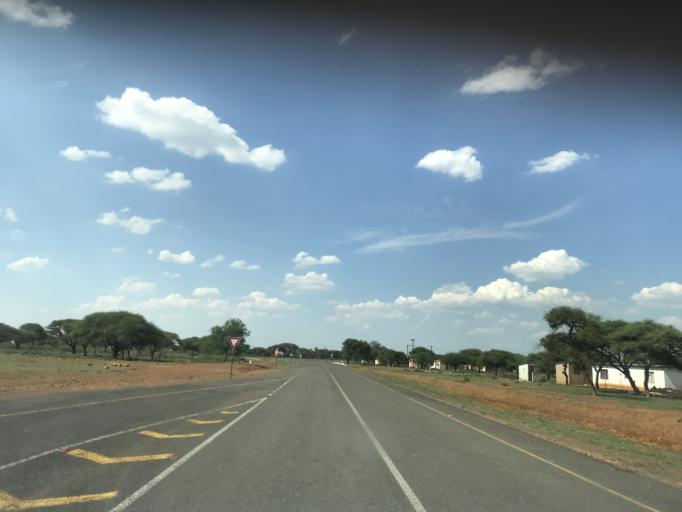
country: BW
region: South East
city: Janeng
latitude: -25.5096
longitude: 25.6306
